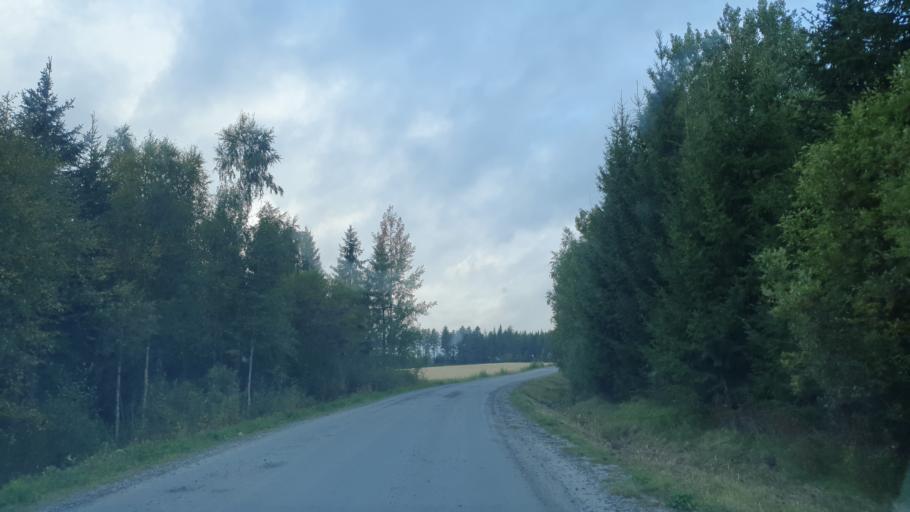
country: FI
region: Kainuu
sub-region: Kehys-Kainuu
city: Kuhmo
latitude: 64.1322
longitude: 29.5863
